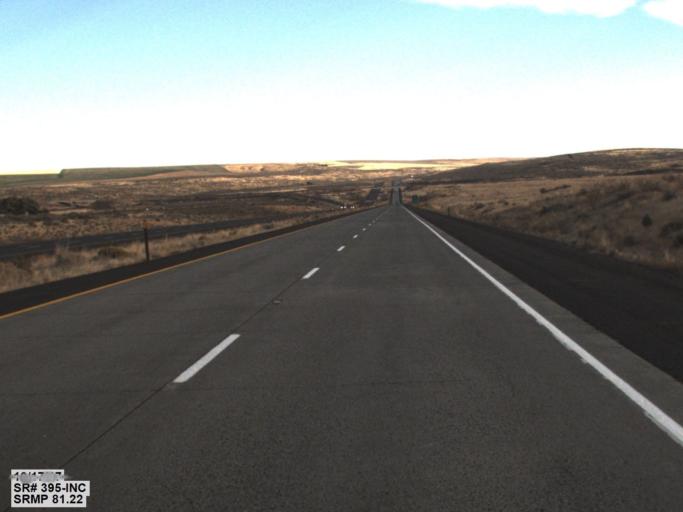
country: US
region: Washington
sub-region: Adams County
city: Ritzville
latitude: 46.9569
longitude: -118.5743
